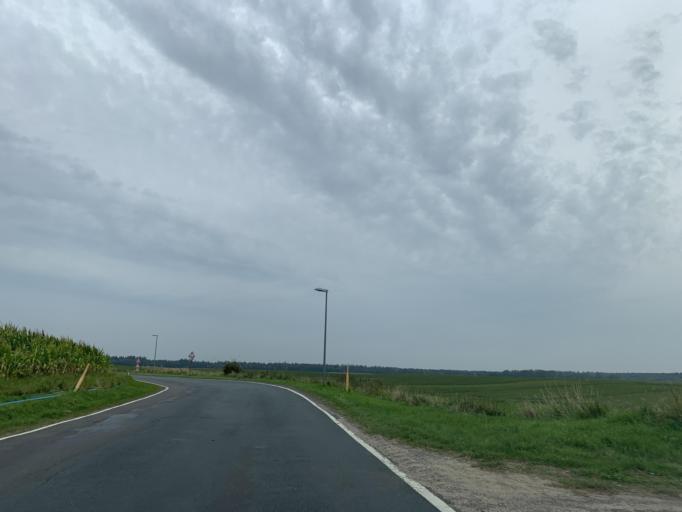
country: DE
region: Mecklenburg-Vorpommern
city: Woldegk
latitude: 53.3332
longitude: 13.6304
